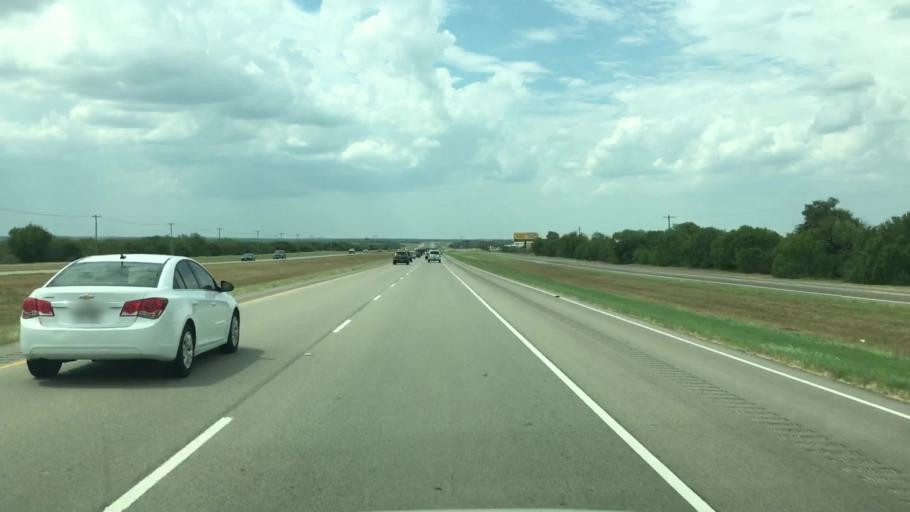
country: US
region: Texas
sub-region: Live Oak County
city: Three Rivers
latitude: 28.5042
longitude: -98.1603
